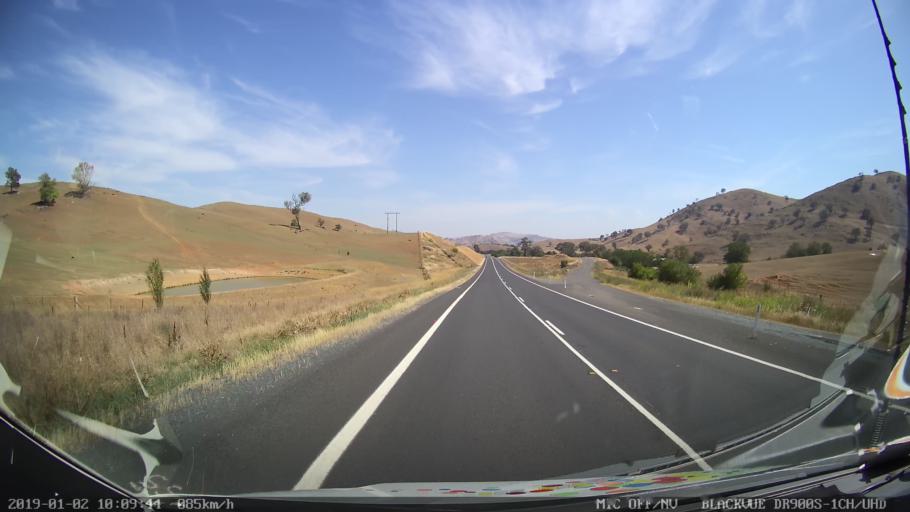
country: AU
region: New South Wales
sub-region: Gundagai
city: Gundagai
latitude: -35.1133
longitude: 148.0977
